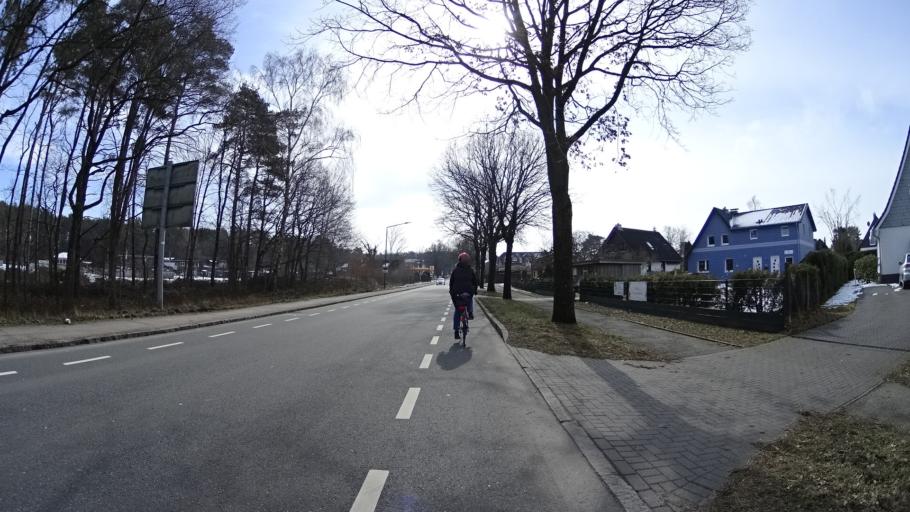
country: DE
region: Schleswig-Holstein
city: Boostedt
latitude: 54.0151
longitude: 10.0185
